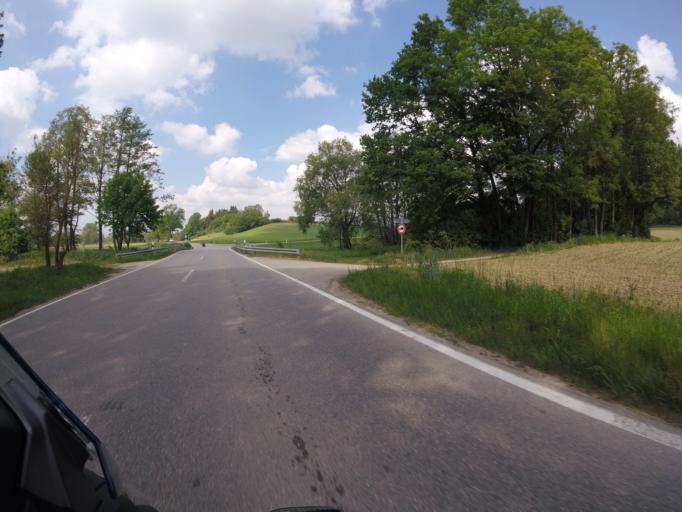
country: DE
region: Bavaria
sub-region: Upper Bavaria
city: Zolling
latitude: 48.4578
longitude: 11.7443
